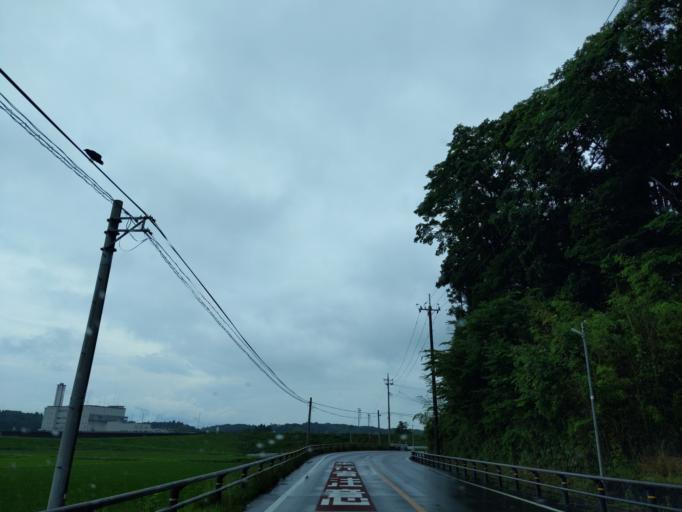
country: JP
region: Fukushima
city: Koriyama
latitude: 37.4256
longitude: 140.4162
